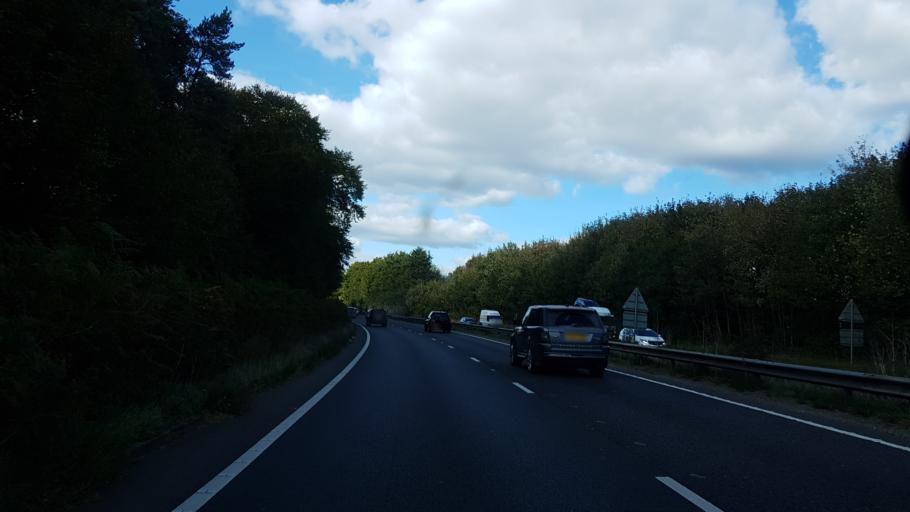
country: GB
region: England
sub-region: Surrey
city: Milford
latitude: 51.1989
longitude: -0.6462
